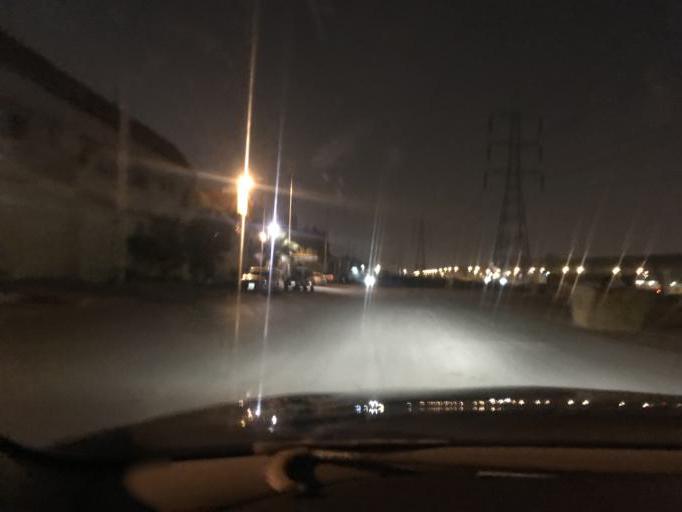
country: SA
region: Ar Riyad
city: Riyadh
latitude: 24.7987
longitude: 46.6924
